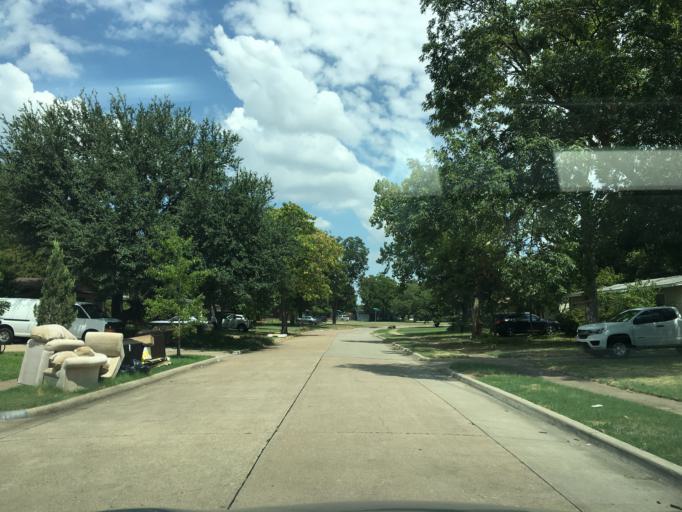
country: US
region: Texas
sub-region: Dallas County
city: Garland
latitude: 32.8611
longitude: -96.6821
